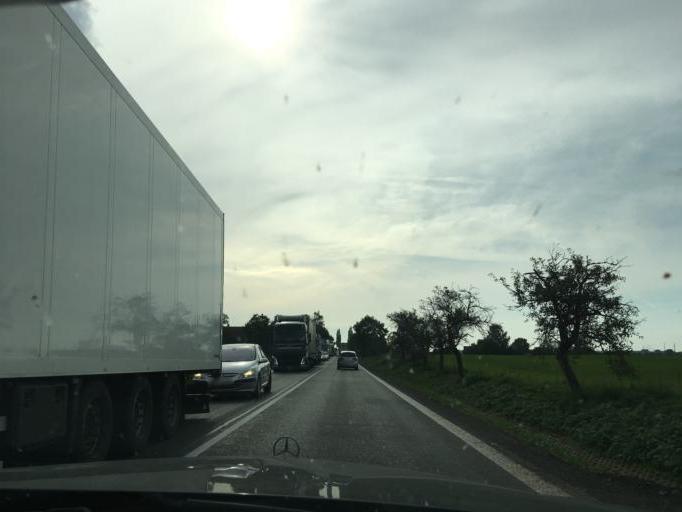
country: CZ
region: Kralovehradecky
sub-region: Okres Hradec Kralove
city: Smirice
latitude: 50.2909
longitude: 15.8338
